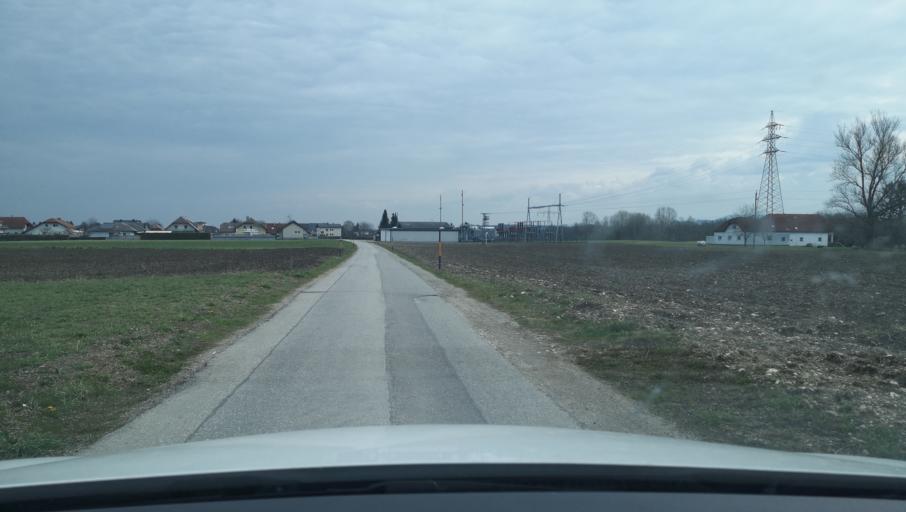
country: AT
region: Lower Austria
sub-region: Politischer Bezirk Amstetten
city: Amstetten
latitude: 48.1126
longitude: 14.9068
